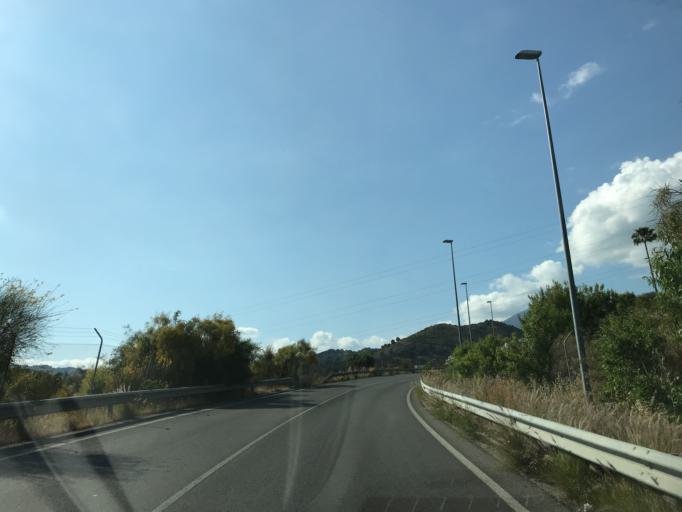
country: ES
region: Andalusia
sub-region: Provincia de Malaga
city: Benahavis
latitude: 36.5008
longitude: -5.0148
